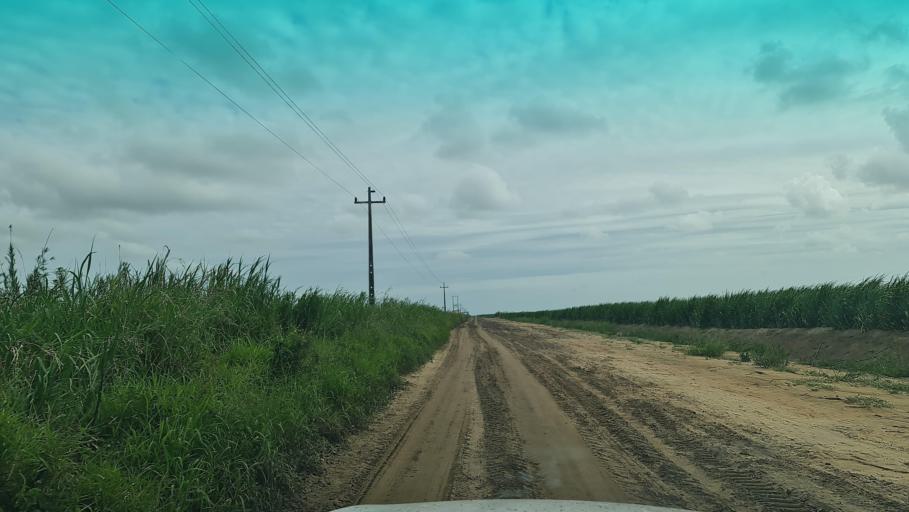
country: MZ
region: Maputo
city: Manhica
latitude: -25.4510
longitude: 32.8392
